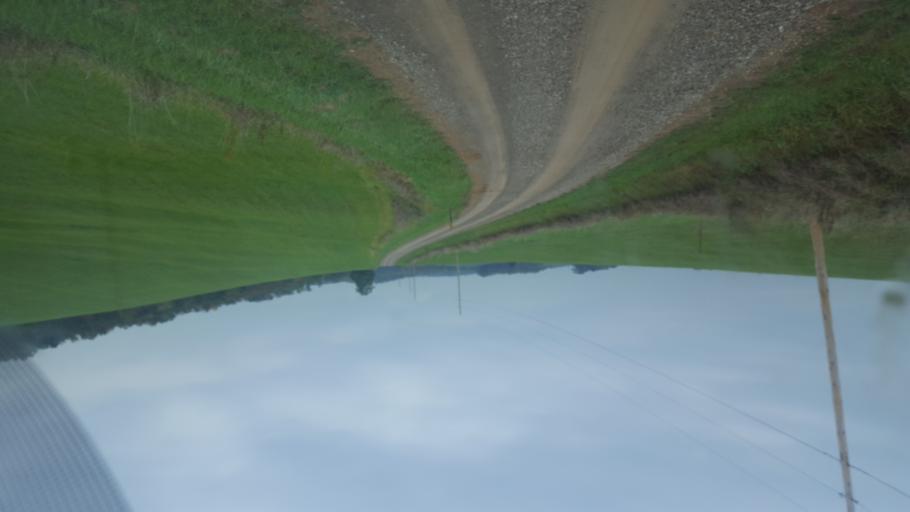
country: US
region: Ohio
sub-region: Knox County
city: Danville
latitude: 40.5057
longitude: -82.3458
